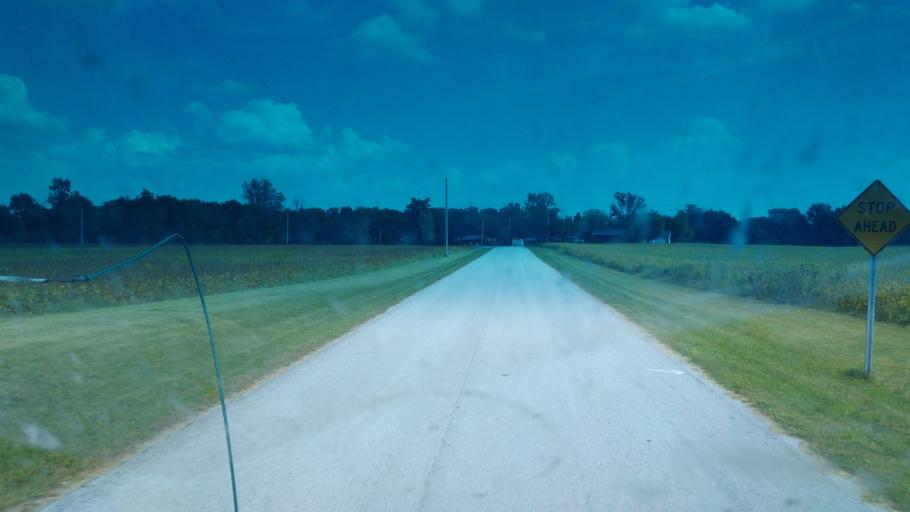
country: US
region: Ohio
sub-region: Hardin County
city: Kenton
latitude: 40.6602
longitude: -83.6766
